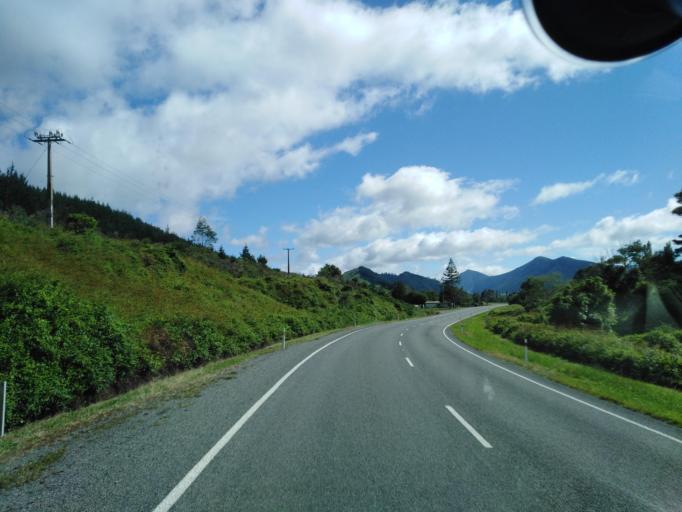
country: NZ
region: Nelson
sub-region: Nelson City
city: Nelson
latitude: -41.2457
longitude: 173.5767
